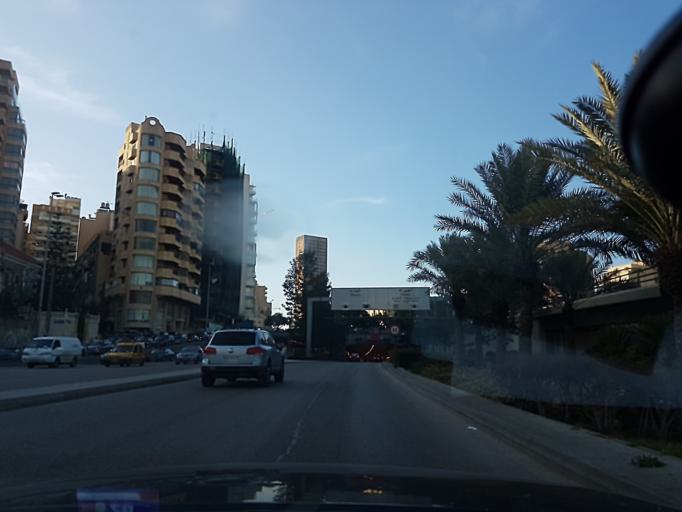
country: LB
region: Beyrouth
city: Beirut
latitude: 33.8936
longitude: 35.5011
